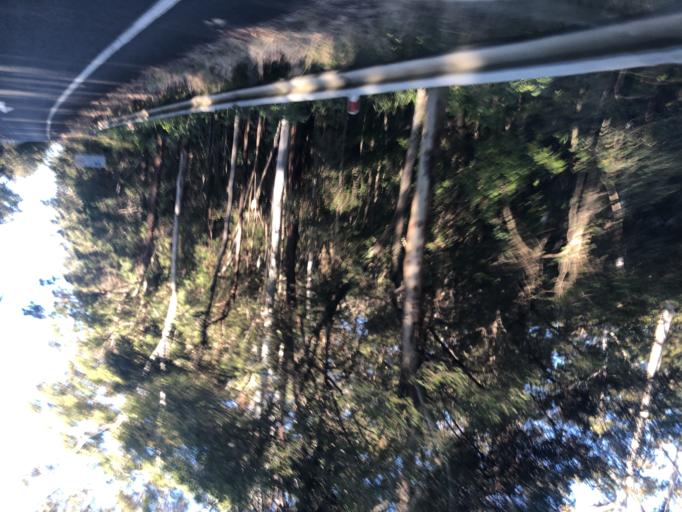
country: AU
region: New South Wales
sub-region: Nambucca Shire
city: Nambucca
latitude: -30.5525
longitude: 153.0078
